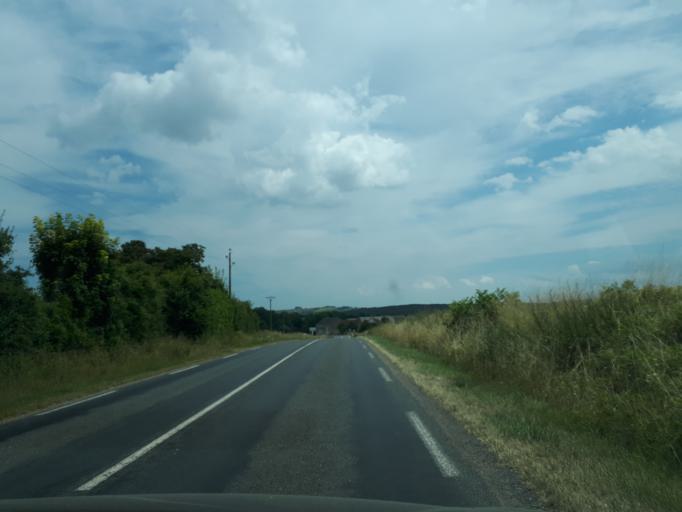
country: FR
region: Centre
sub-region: Departement du Cher
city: Rians
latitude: 47.2185
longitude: 2.6251
